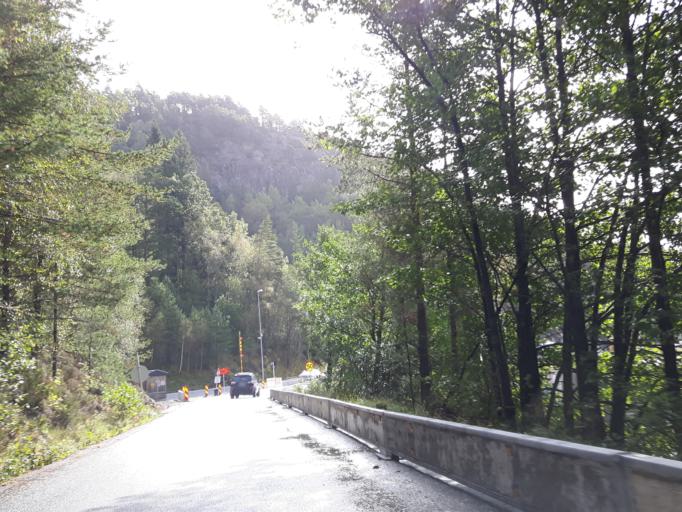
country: NO
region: Vest-Agder
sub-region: Flekkefjord
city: Flekkefjord
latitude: 58.3904
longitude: 6.6275
